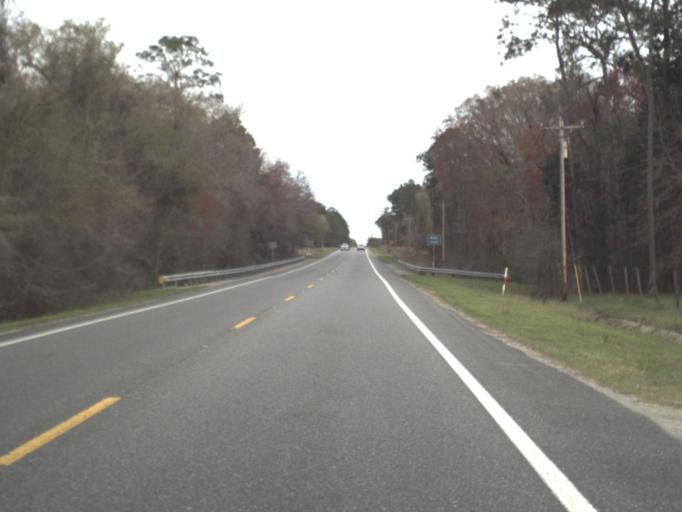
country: US
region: Florida
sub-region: Wakulla County
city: Crawfordville
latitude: 30.2788
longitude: -84.3871
